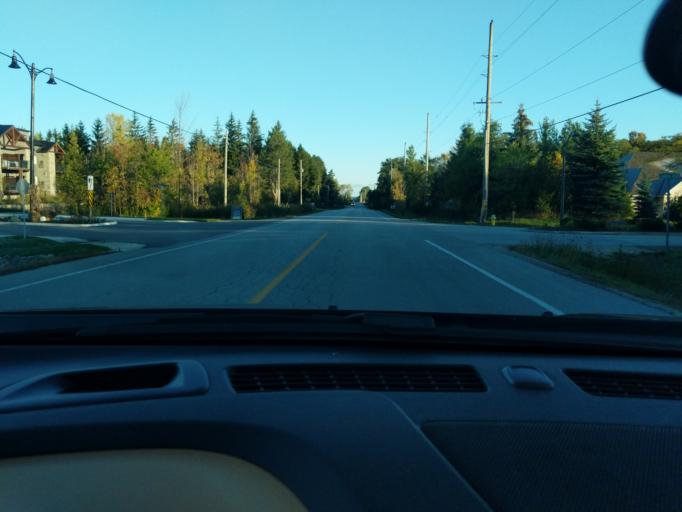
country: CA
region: Ontario
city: Collingwood
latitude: 44.4997
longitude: -80.2858
